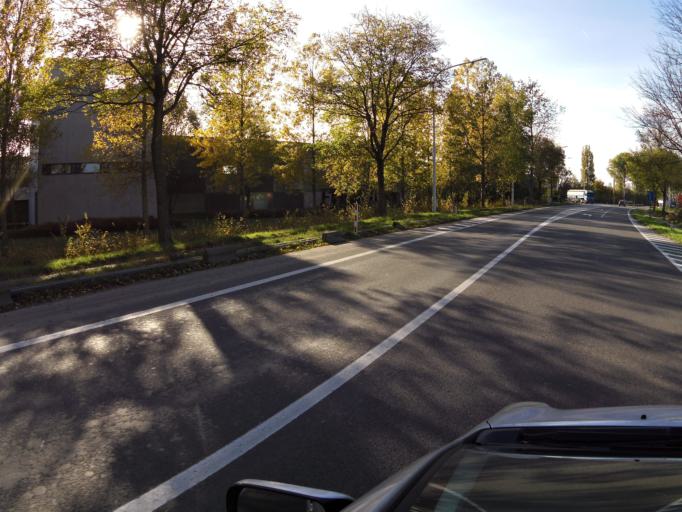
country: BE
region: Flanders
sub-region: Provincie West-Vlaanderen
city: Veurne
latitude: 51.0729
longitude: 2.6918
